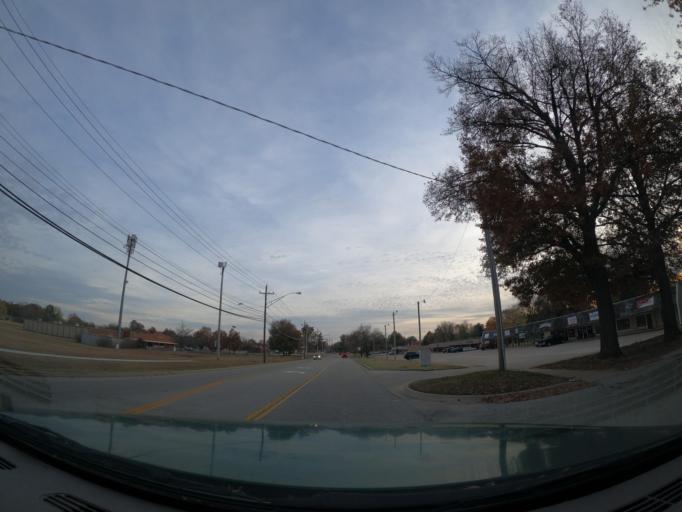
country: US
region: Oklahoma
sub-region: Tulsa County
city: Broken Arrow
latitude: 35.9762
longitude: -95.7974
